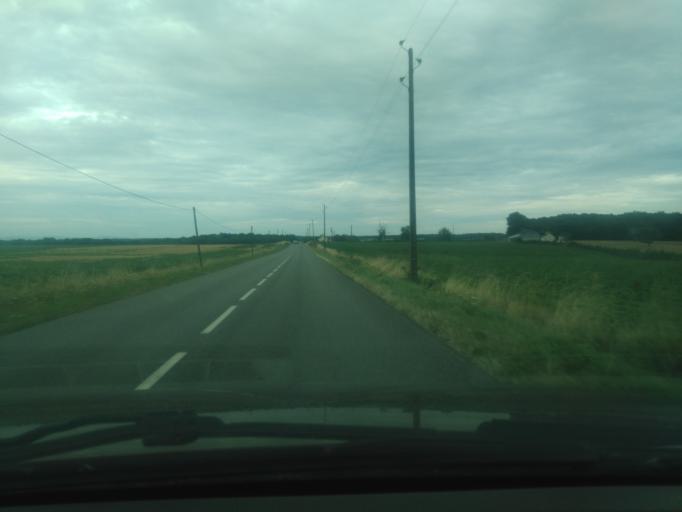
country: FR
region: Bourgogne
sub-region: Departement de la Nievre
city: Dornes
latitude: 46.7730
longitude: 3.3434
